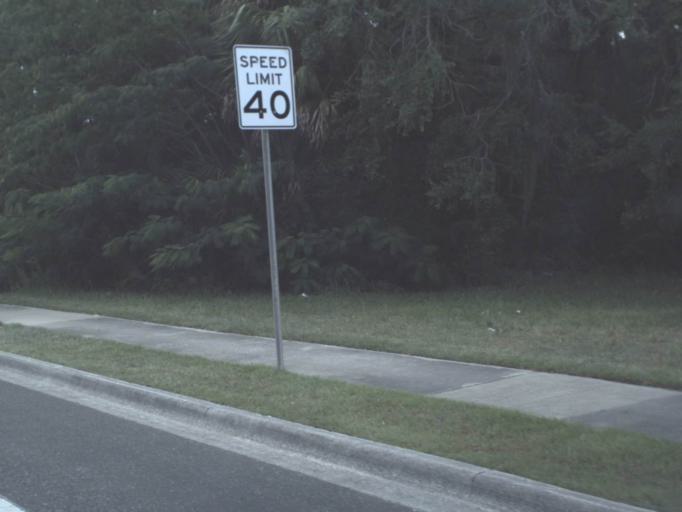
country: US
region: Florida
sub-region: Taylor County
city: Perry
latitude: 30.1156
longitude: -83.5893
